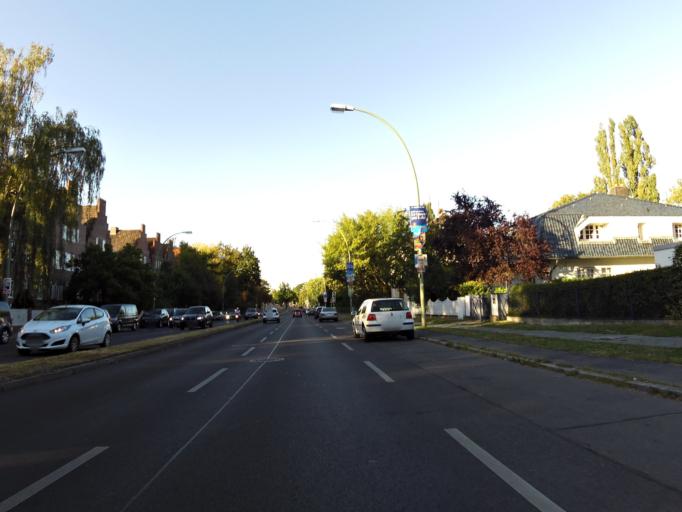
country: DE
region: Berlin
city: Zehlendorf Bezirk
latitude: 52.4431
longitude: 13.2662
